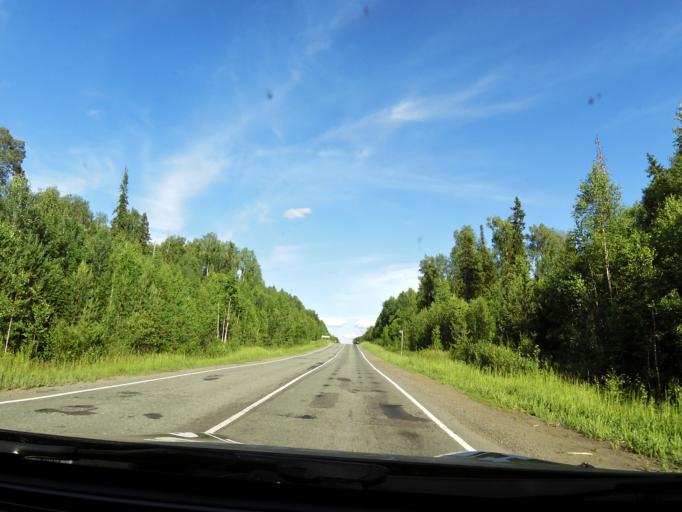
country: RU
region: Kirov
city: Chernaya Kholunitsa
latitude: 58.8633
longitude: 51.5931
